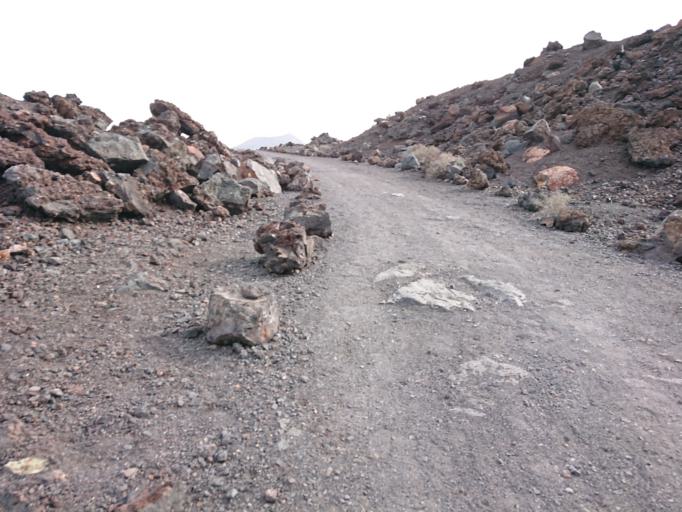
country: ES
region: Canary Islands
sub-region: Provincia de Las Palmas
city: Tinajo
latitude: 29.0090
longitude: -13.6768
